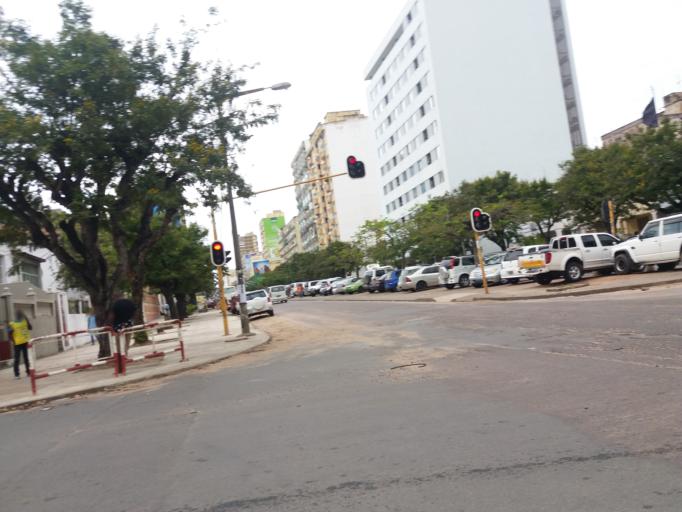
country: MZ
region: Maputo City
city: Maputo
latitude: -25.9668
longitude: 32.5756
